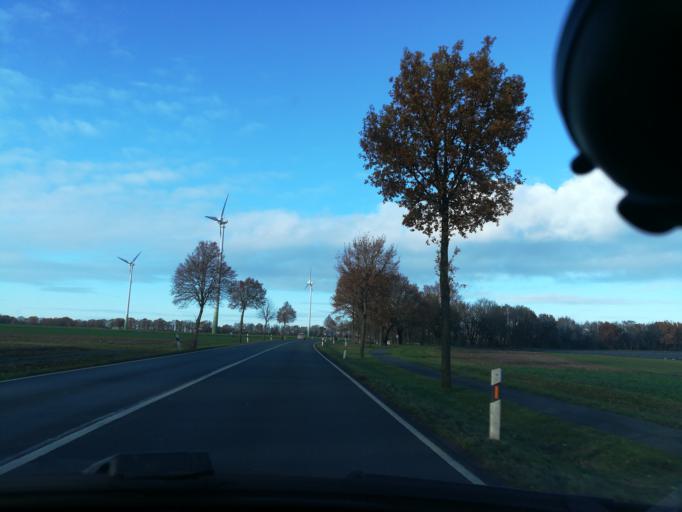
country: DE
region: Lower Saxony
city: Uchte
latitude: 52.4761
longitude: 8.8981
